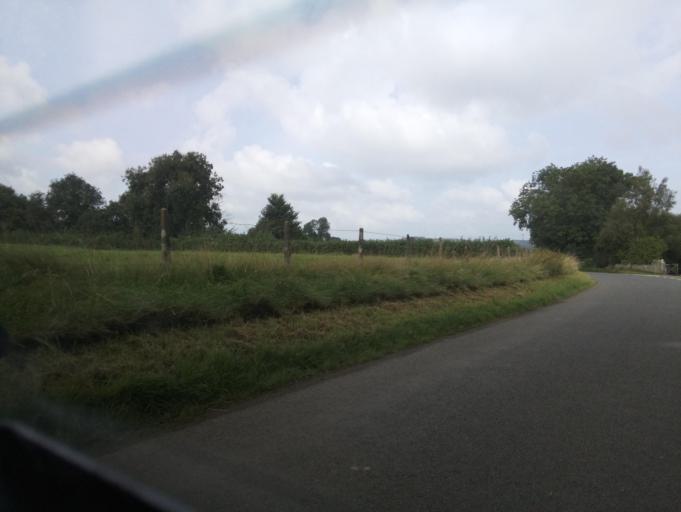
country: GB
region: England
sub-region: Bath and North East Somerset
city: Cameley
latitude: 51.2657
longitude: -2.5766
